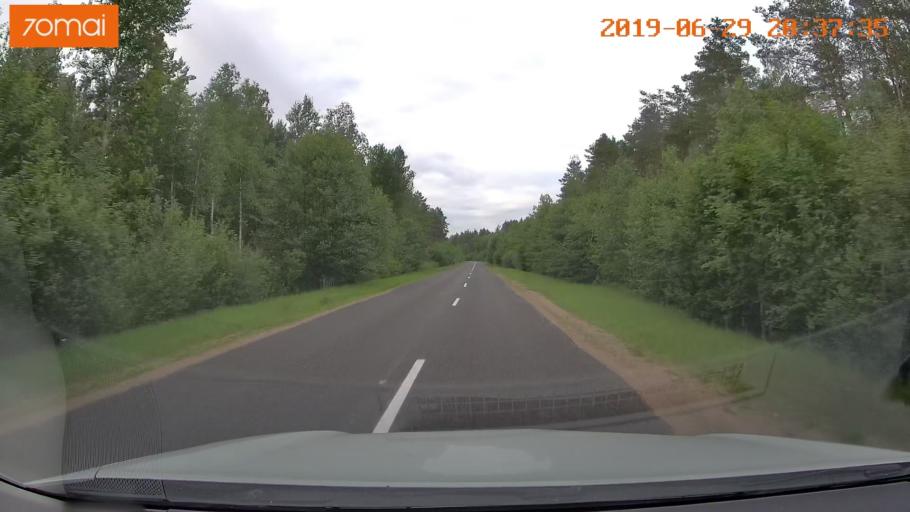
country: BY
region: Brest
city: Hantsavichy
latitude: 52.5398
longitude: 26.3650
